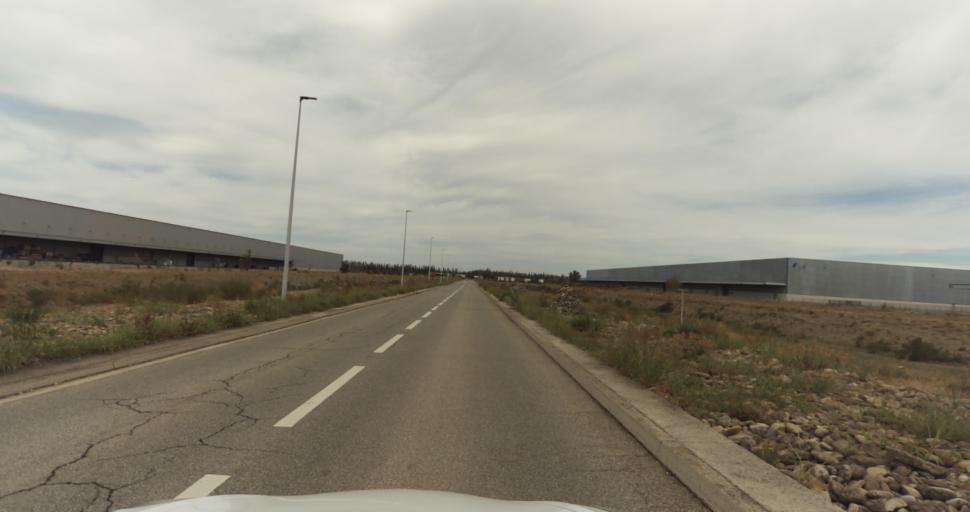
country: FR
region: Provence-Alpes-Cote d'Azur
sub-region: Departement des Bouches-du-Rhone
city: Miramas
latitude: 43.6100
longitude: 4.9997
